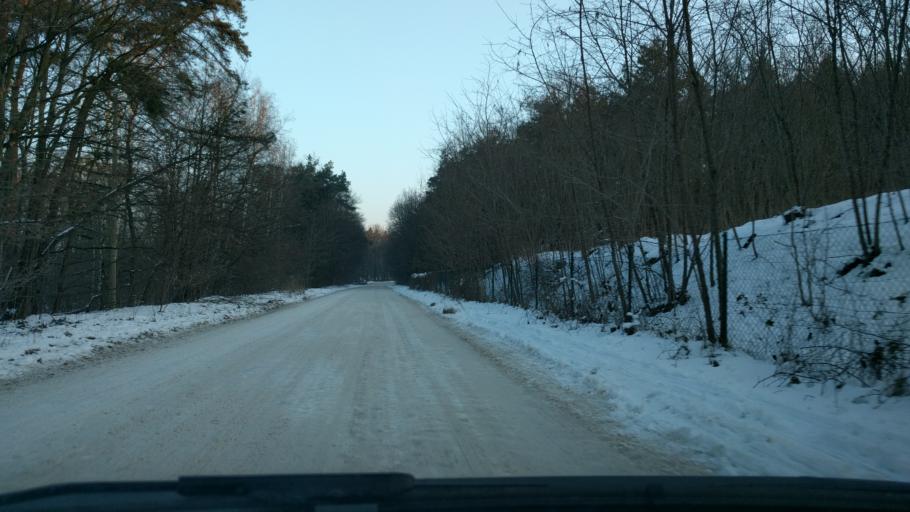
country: DE
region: Saxony
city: Albertstadt
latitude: 51.0795
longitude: 13.7744
